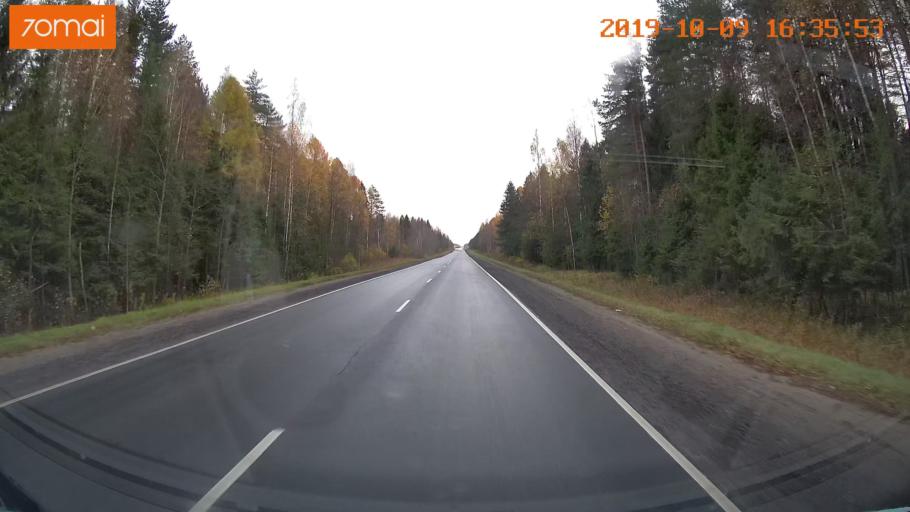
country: RU
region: Kostroma
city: Volgorechensk
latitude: 57.5492
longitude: 41.0062
